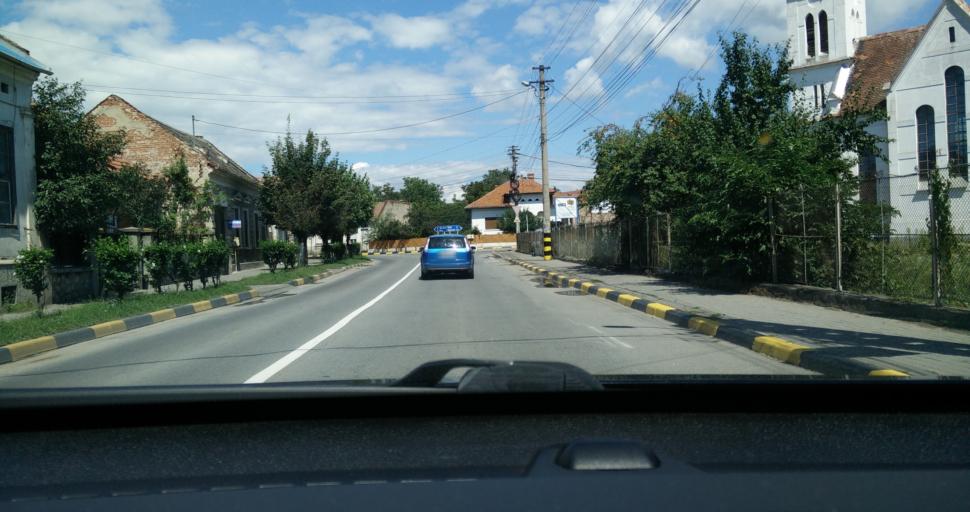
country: RO
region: Alba
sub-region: Municipiul Sebes
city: Sebes
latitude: 45.9549
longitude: 23.5660
